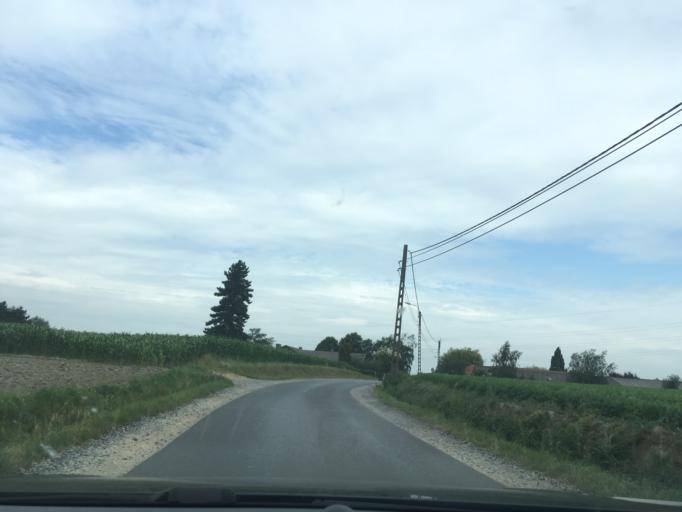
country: BE
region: Flanders
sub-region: Provincie West-Vlaanderen
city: Pittem
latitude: 50.9849
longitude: 3.2834
